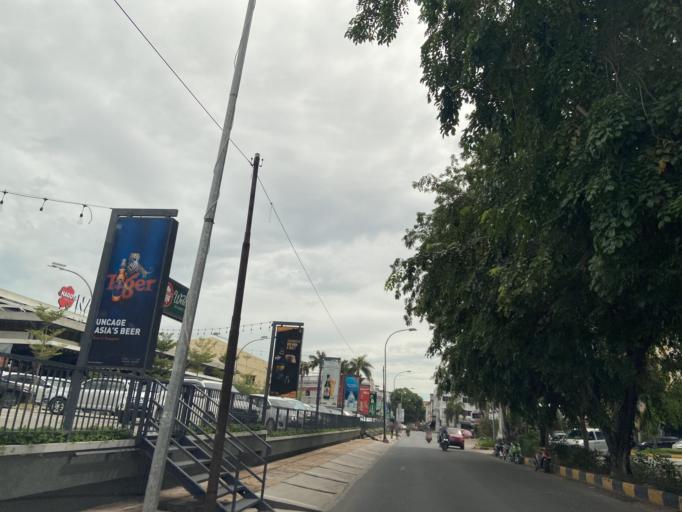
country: SG
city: Singapore
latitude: 1.1421
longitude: 104.0072
